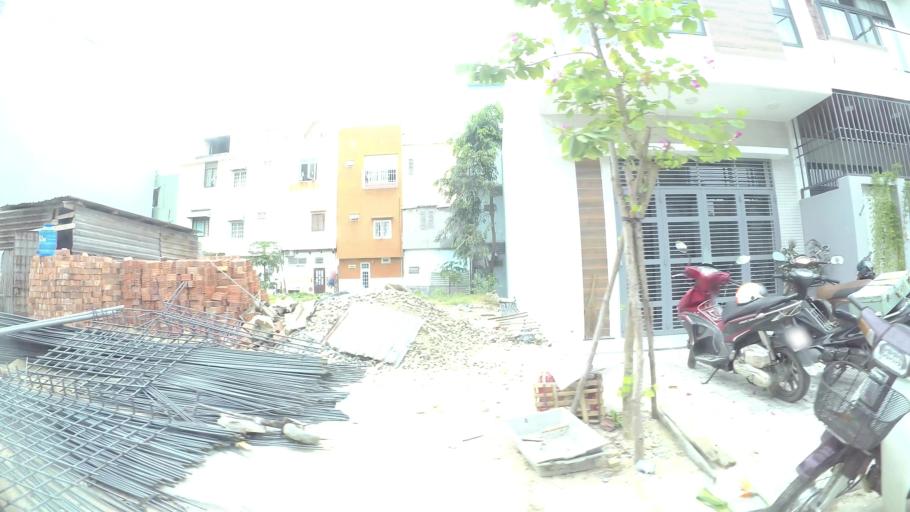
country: VN
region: Da Nang
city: Da Nang
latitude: 16.0792
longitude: 108.2135
